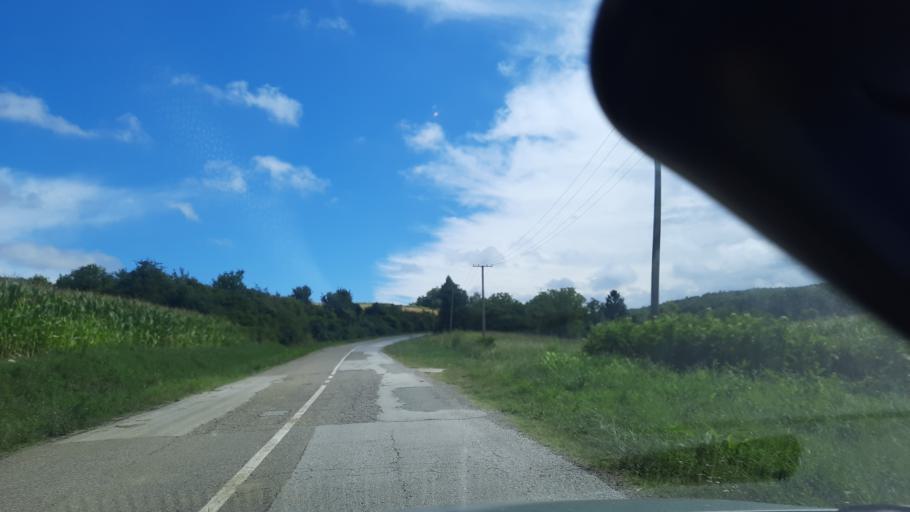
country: RS
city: Glozan
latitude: 45.1673
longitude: 19.5880
